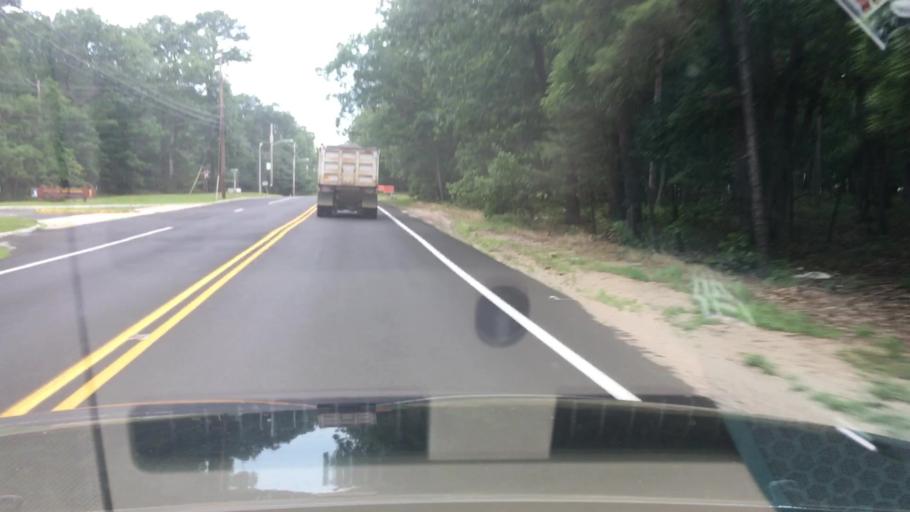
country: US
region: New Jersey
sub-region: Ocean County
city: Lakehurst
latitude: 40.0580
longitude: -74.3521
